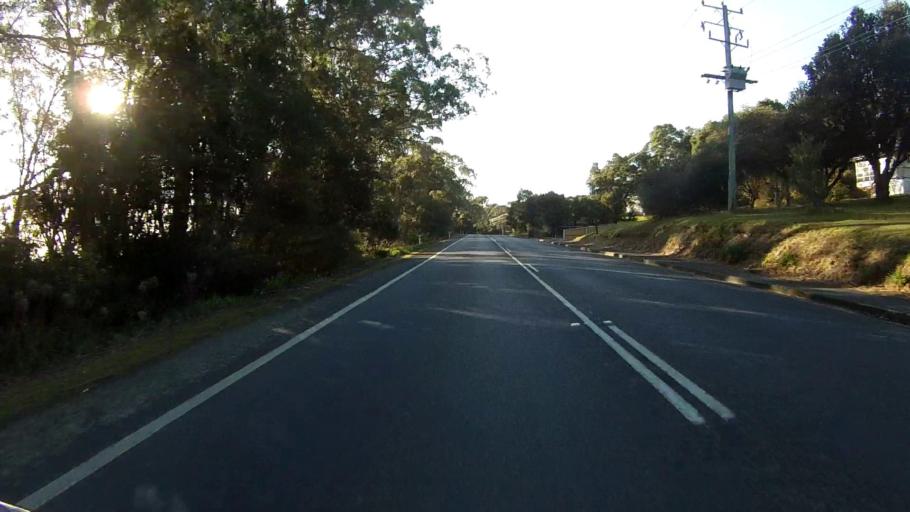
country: AU
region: Tasmania
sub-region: Clarence
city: Sandford
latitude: -43.0440
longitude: 147.8657
